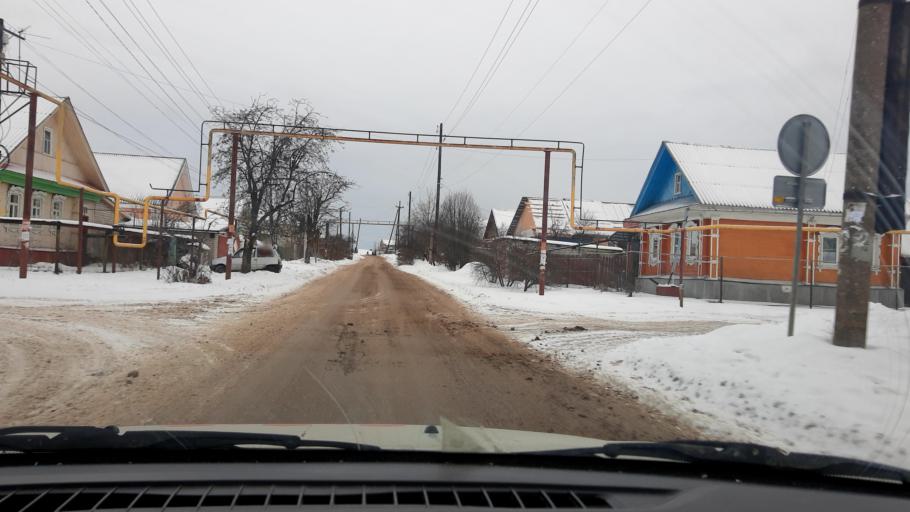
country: RU
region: Nizjnij Novgorod
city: Gorodets
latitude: 56.6590
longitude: 43.4804
